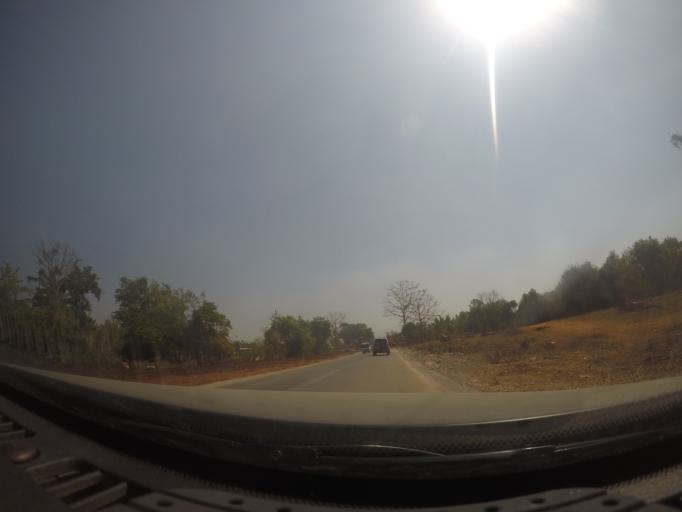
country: MM
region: Shan
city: Taunggyi
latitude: 20.7789
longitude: 97.1455
